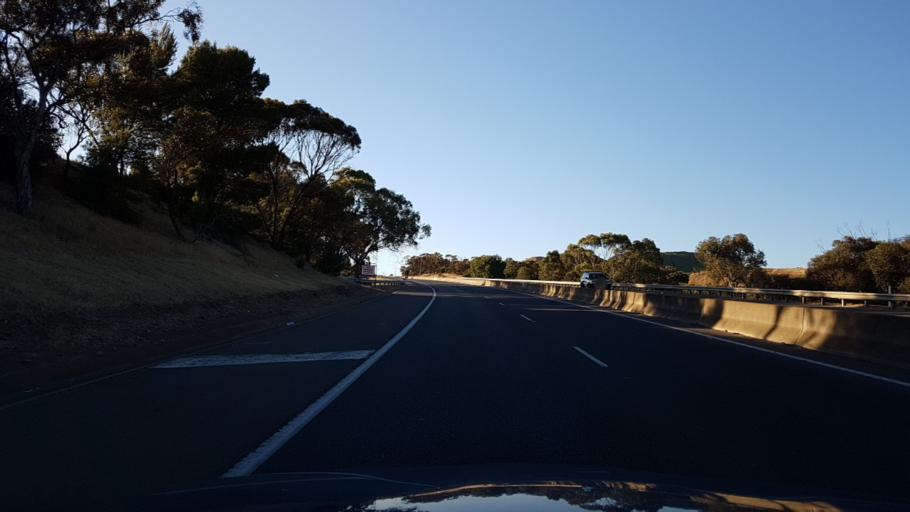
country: AU
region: South Australia
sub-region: Onkaparinga
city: Reynella
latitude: -35.0964
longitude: 138.4966
